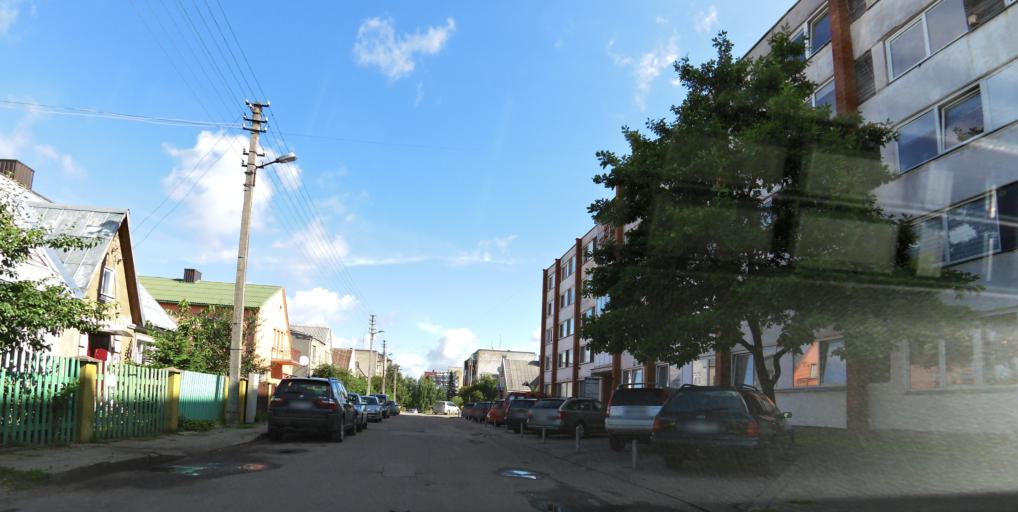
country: LT
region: Vilnius County
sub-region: Vilnius
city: Vilnius
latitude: 54.7092
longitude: 25.2812
